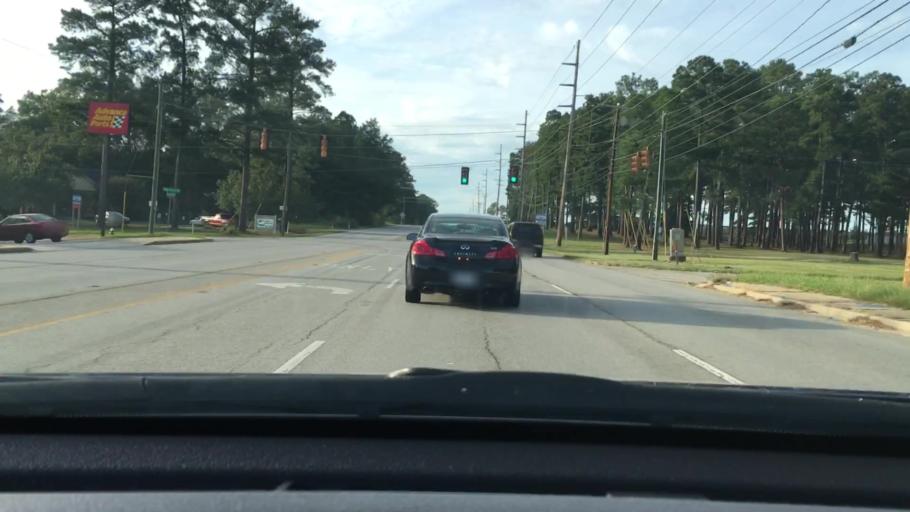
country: US
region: South Carolina
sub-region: Lexington County
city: Saint Andrews
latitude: 34.0705
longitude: -81.1199
